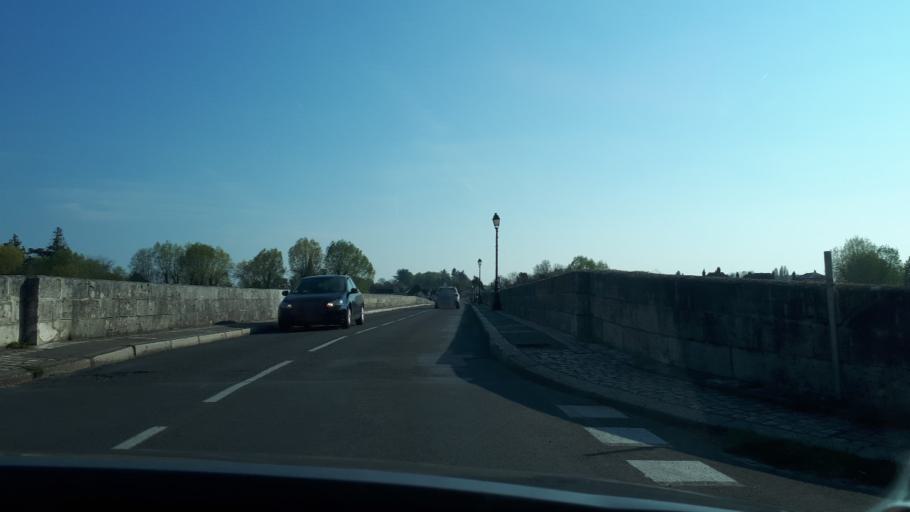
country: FR
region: Centre
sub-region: Departement d'Indre-et-Loire
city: Blere
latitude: 47.3318
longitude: 0.9918
